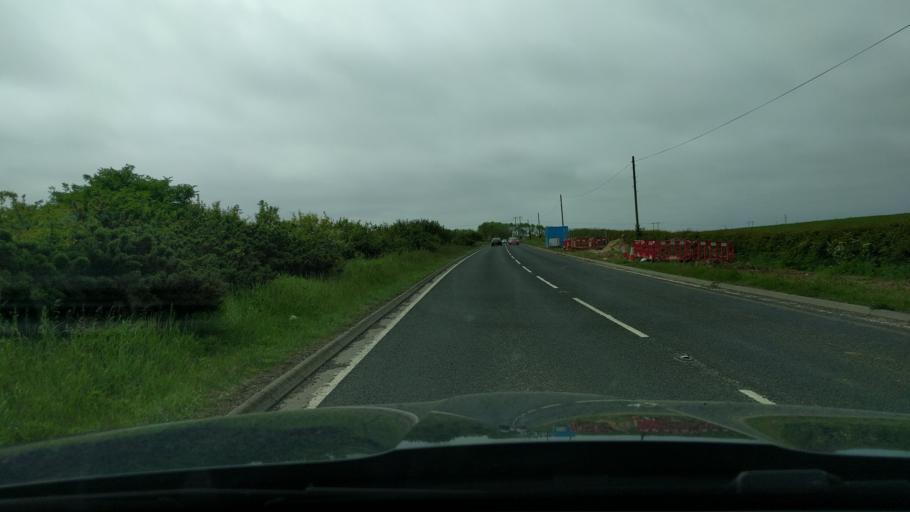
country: GB
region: England
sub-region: Northumberland
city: East Chevington
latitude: 55.2396
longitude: -1.5926
